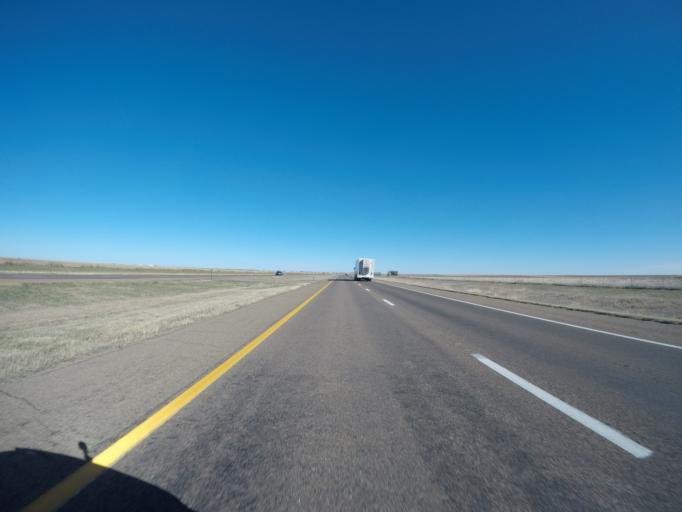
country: US
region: Kansas
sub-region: Thomas County
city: Colby
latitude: 39.3649
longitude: -101.1041
